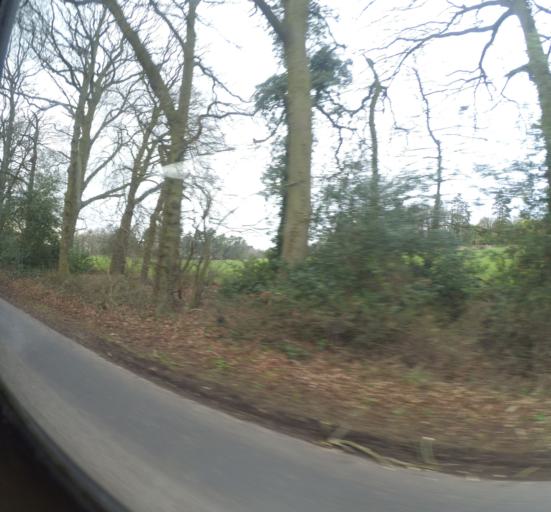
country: GB
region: England
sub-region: Warwickshire
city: Long Lawford
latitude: 52.4102
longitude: -1.3323
